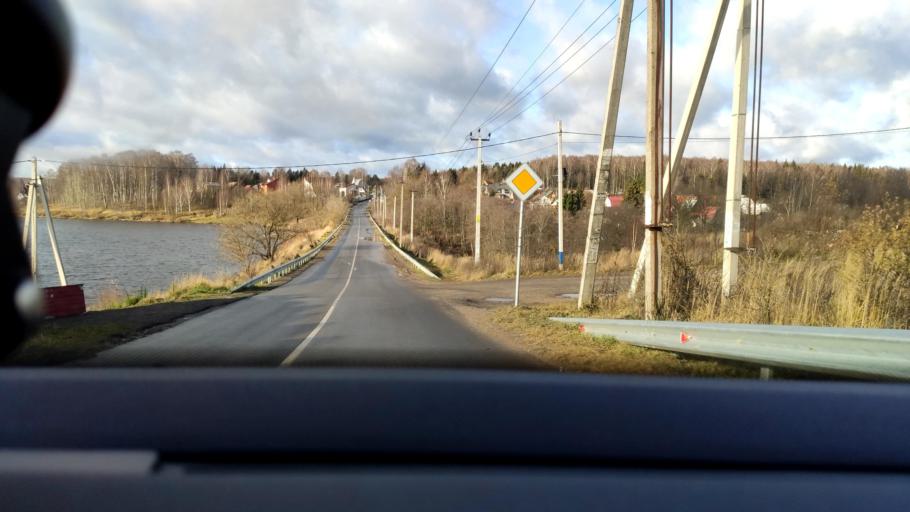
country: RU
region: Moskovskaya
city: Yermolino
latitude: 56.1568
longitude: 37.4793
